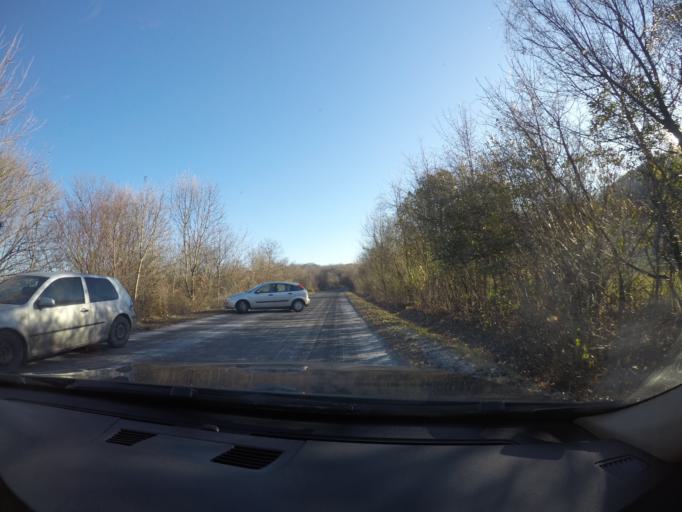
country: HU
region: Pest
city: Visegrad
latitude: 47.8000
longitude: 18.9919
